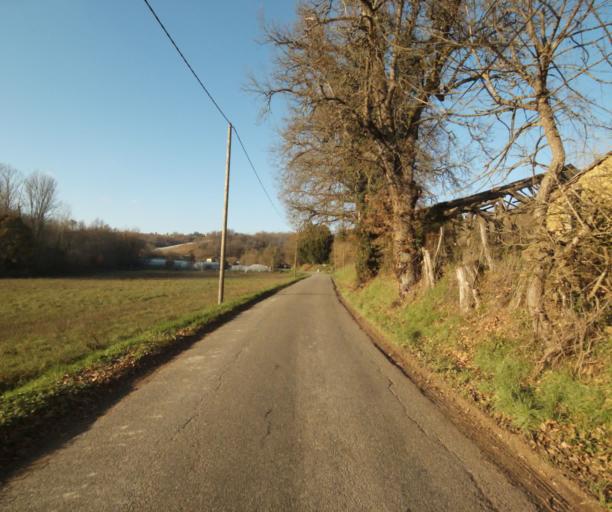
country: FR
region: Midi-Pyrenees
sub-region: Departement du Tarn-et-Garonne
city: Moissac
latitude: 44.1262
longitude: 1.1316
